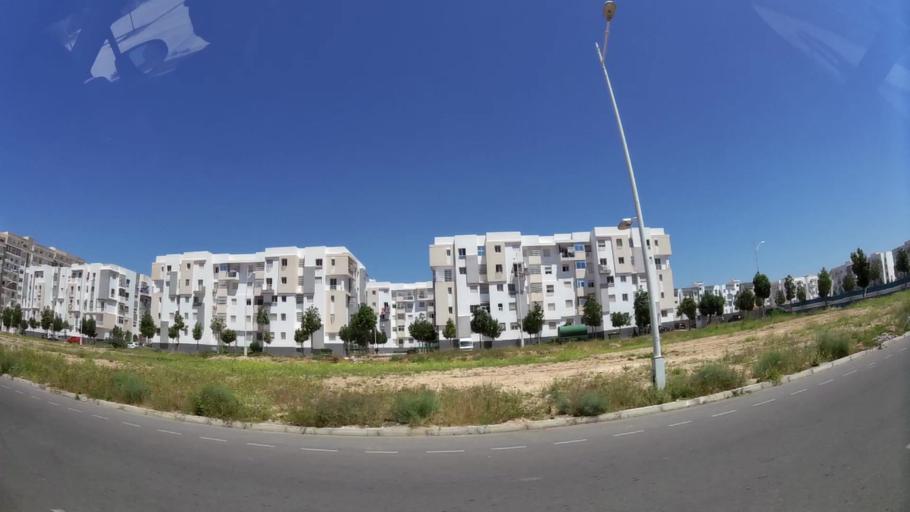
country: MA
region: Oued ed Dahab-Lagouira
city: Dakhla
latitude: 30.4366
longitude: -9.5613
